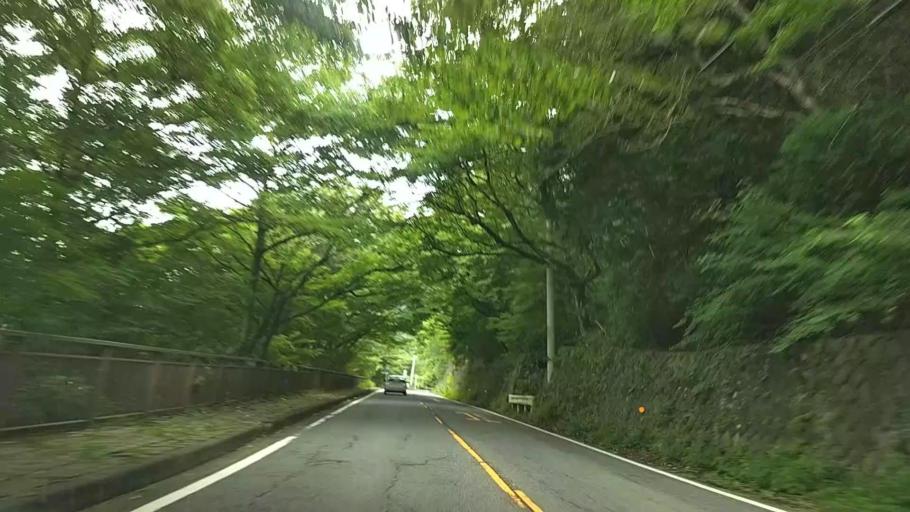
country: JP
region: Kanagawa
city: Hakone
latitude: 35.2049
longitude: 139.0546
